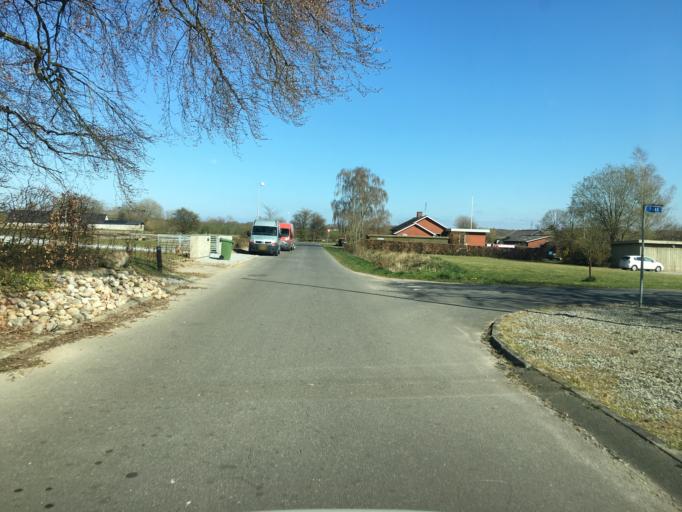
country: DK
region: South Denmark
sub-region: Aabenraa Kommune
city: Rodekro
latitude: 55.0272
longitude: 9.3459
